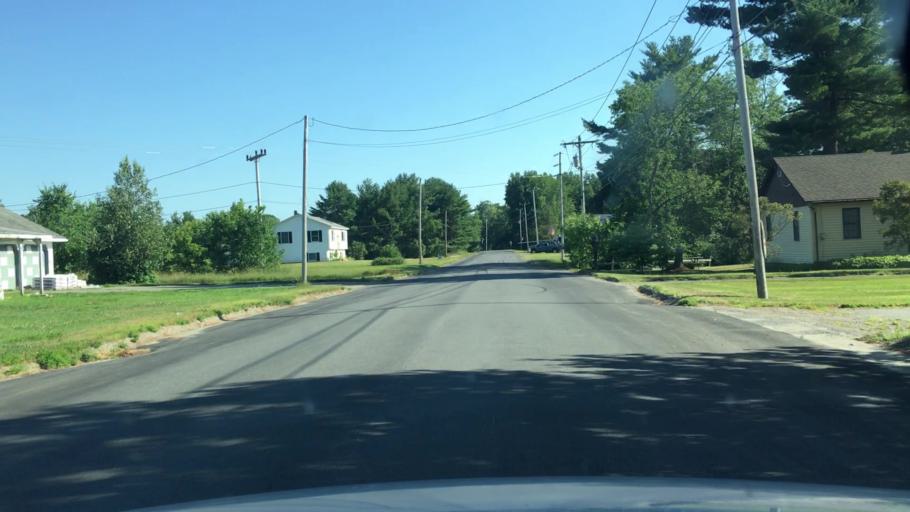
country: US
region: Maine
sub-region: Penobscot County
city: Howland
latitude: 45.2339
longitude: -68.6490
